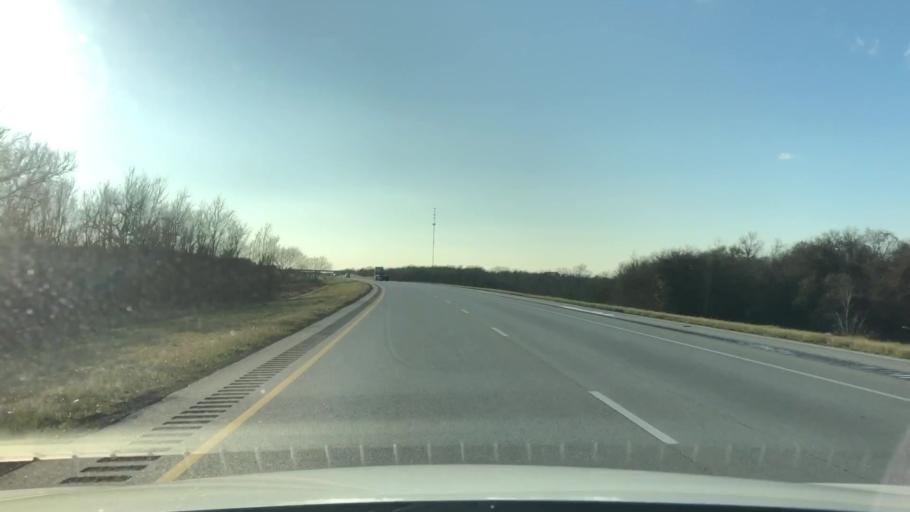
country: US
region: Texas
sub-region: Fayette County
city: Flatonia
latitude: 29.6965
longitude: -97.1440
